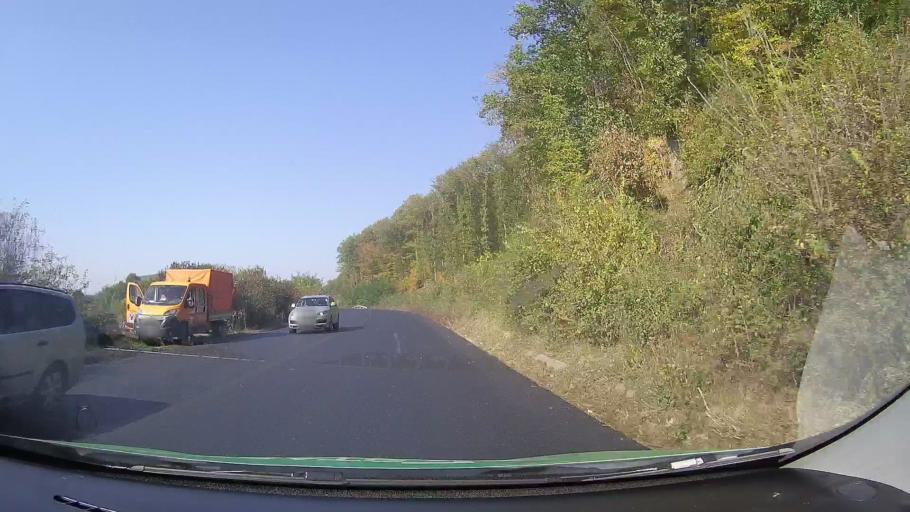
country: RO
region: Hunedoara
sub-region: Comuna Zam
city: Zam
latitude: 46.0162
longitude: 22.4204
